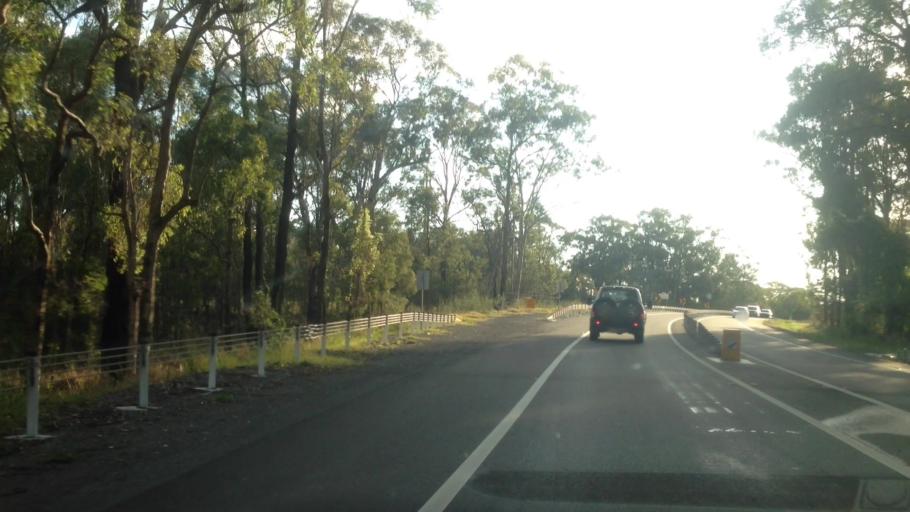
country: AU
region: New South Wales
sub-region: Cessnock
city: Heddon Greta
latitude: -32.8306
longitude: 151.5104
